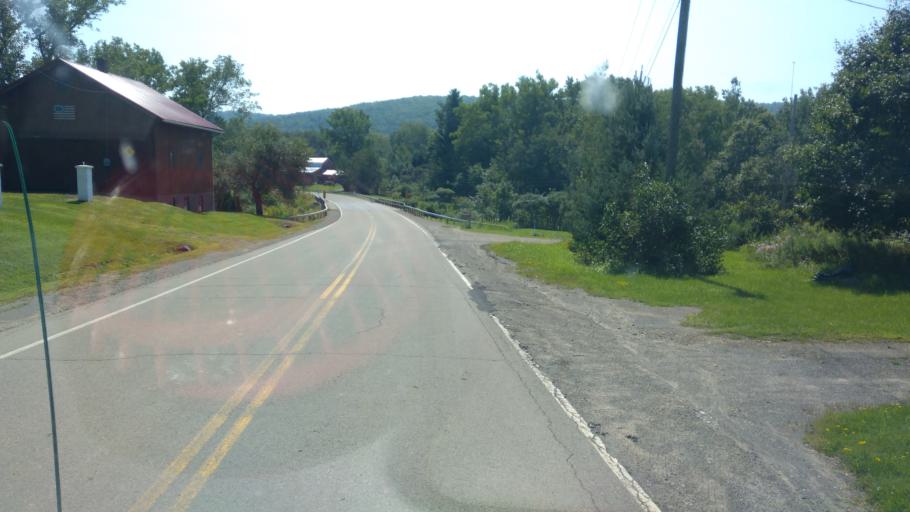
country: US
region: New York
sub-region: Allegany County
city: Belmont
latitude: 42.3021
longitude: -77.9879
